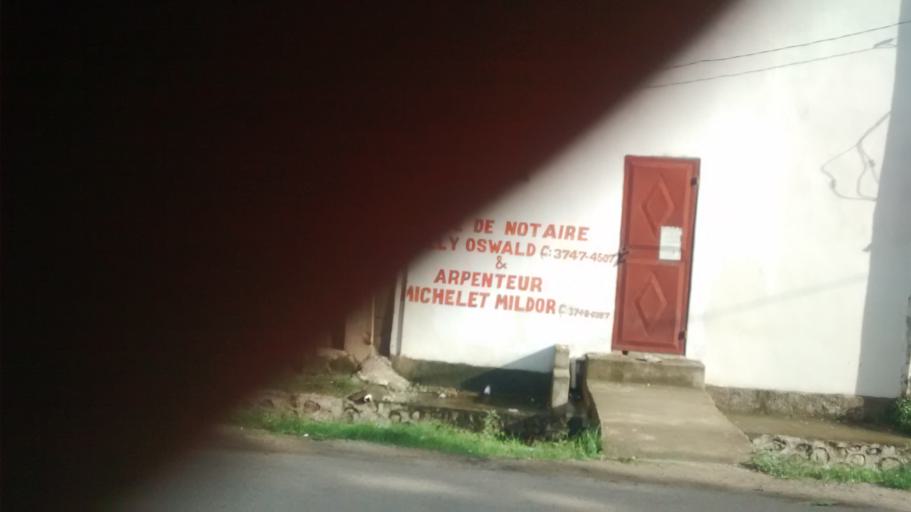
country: HT
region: Nord
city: Limonade
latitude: 19.6701
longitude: -72.1268
